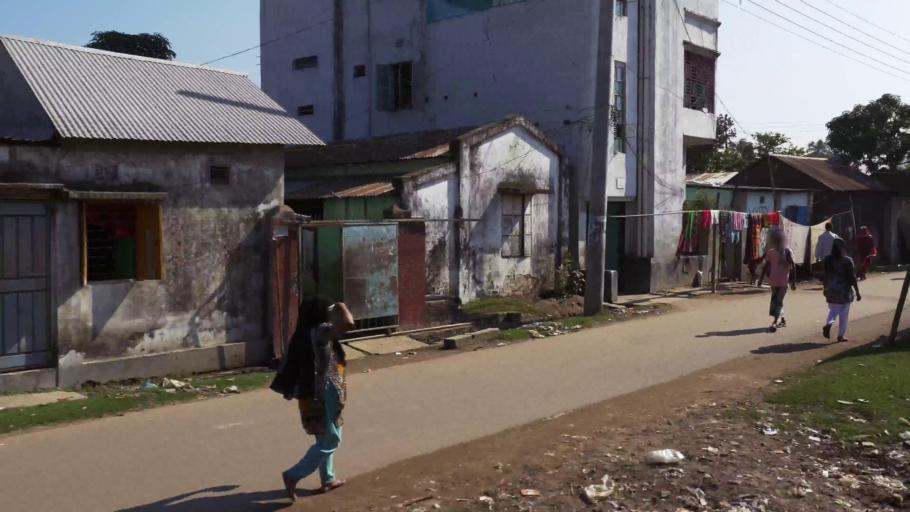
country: BD
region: Dhaka
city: Mymensingh
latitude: 24.6247
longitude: 90.4699
